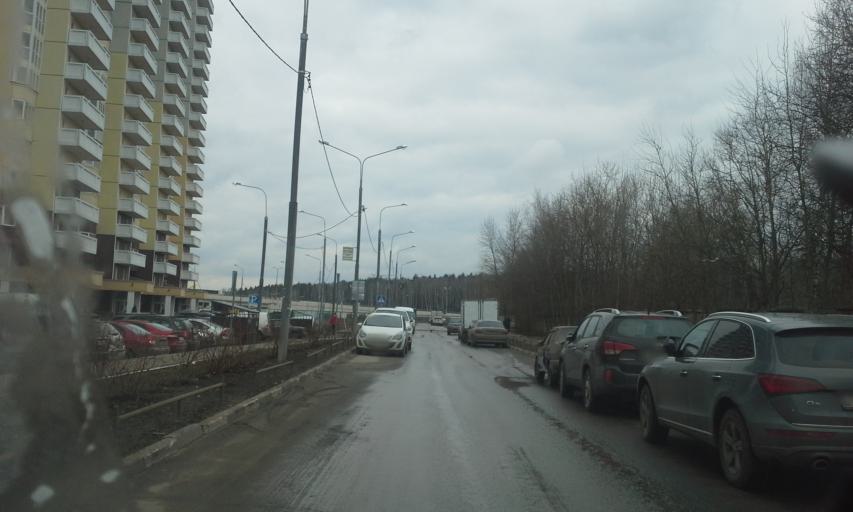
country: RU
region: Moskovskaya
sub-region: Leninskiy Rayon
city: Vnukovo
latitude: 55.6256
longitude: 37.3149
